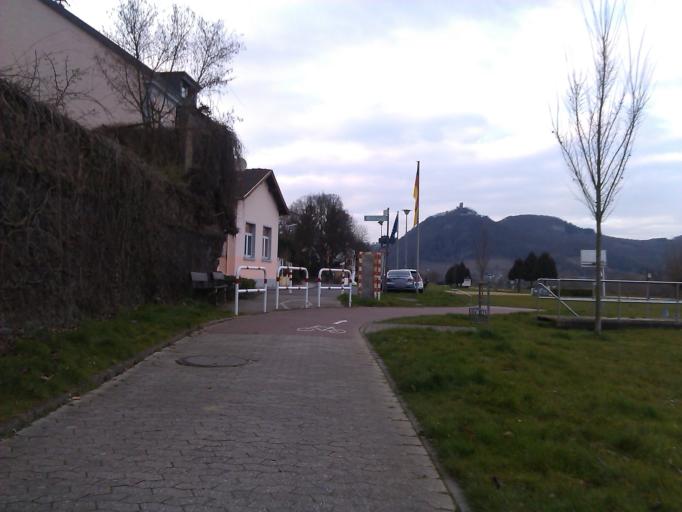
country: DE
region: North Rhine-Westphalia
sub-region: Regierungsbezirk Koln
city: Bad Honnef
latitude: 50.6439
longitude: 7.2064
